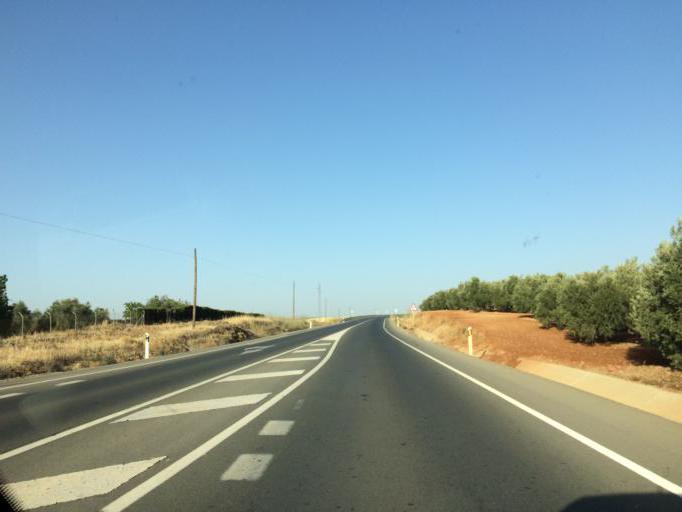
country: ES
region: Andalusia
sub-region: Provincia de Malaga
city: Humilladero
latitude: 37.0608
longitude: -4.7261
